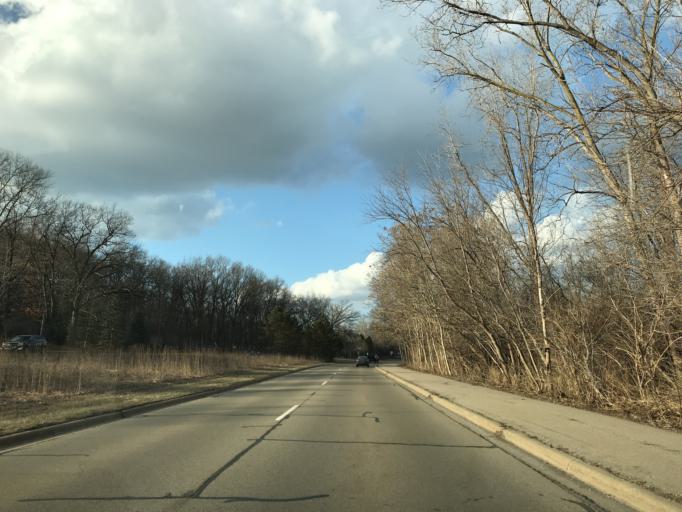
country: US
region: Michigan
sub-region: Washtenaw County
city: Ann Arbor
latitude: 42.2855
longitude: -83.7023
